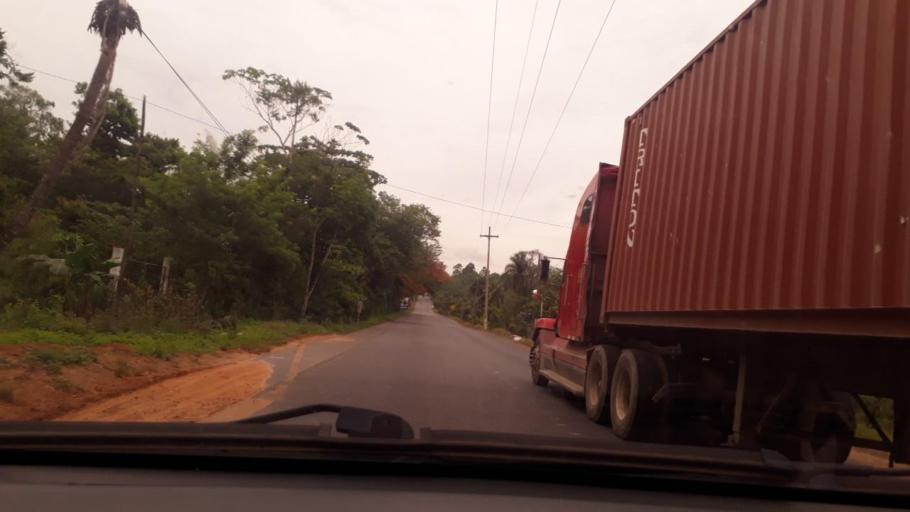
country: GT
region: Izabal
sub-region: Municipio de Puerto Barrios
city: Puerto Barrios
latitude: 15.6011
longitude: -88.5699
